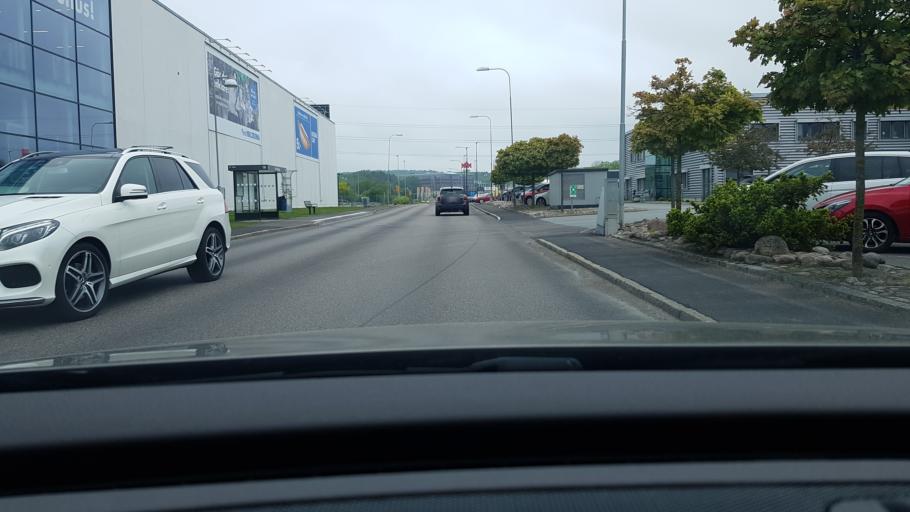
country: SE
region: Vaestra Goetaland
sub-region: Molndal
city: Moelndal
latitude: 57.6433
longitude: 11.9556
